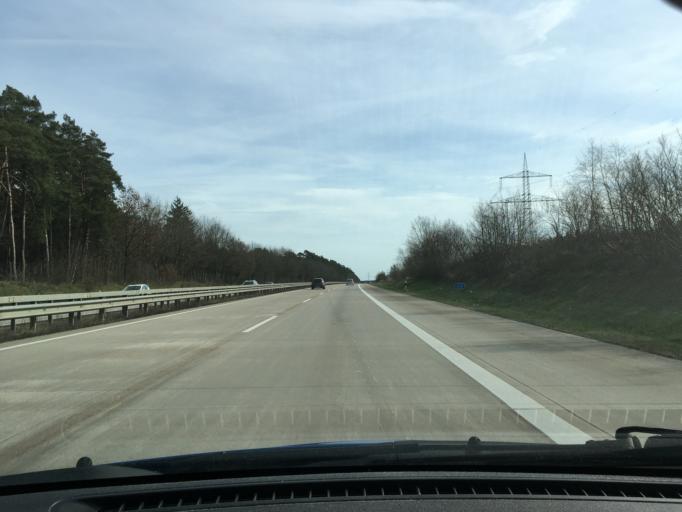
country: DE
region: Schleswig-Holstein
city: Gottin
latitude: 53.5464
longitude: 10.7021
